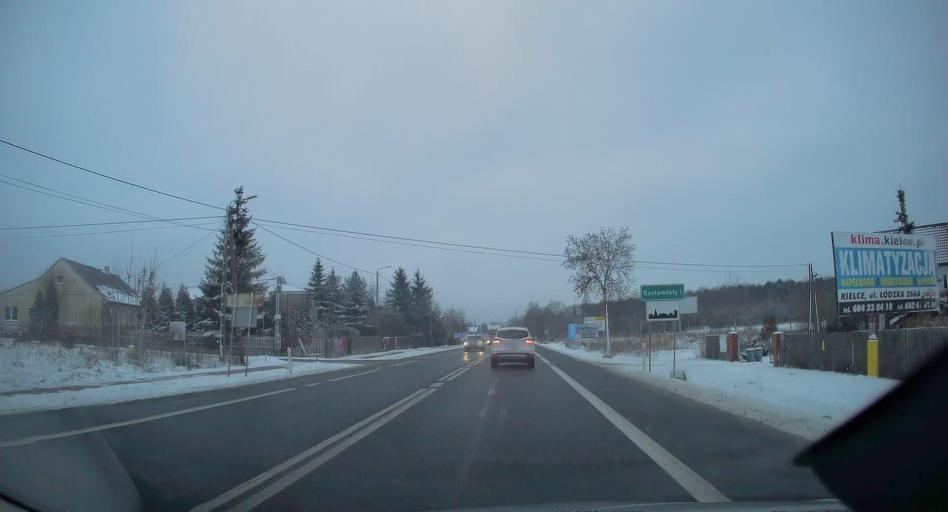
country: PL
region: Swietokrzyskie
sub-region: Powiat kielecki
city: Kostomloty Drugie
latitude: 50.9183
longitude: 20.5710
